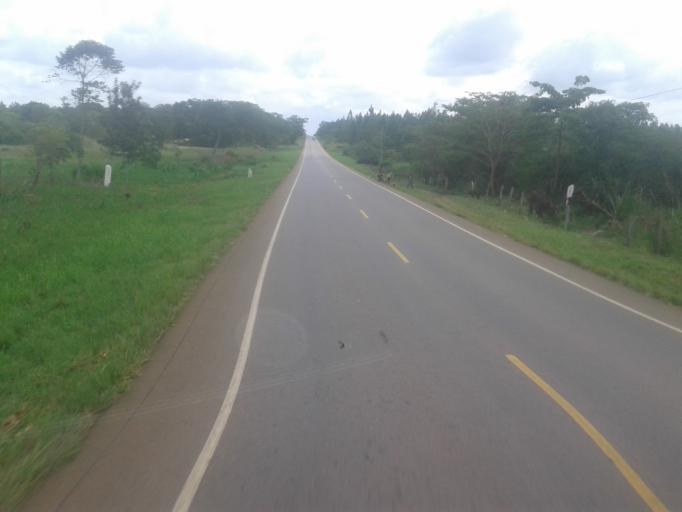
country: UG
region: Central Region
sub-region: Nakasongola District
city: Nakasongola
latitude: 1.0914
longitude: 32.4662
